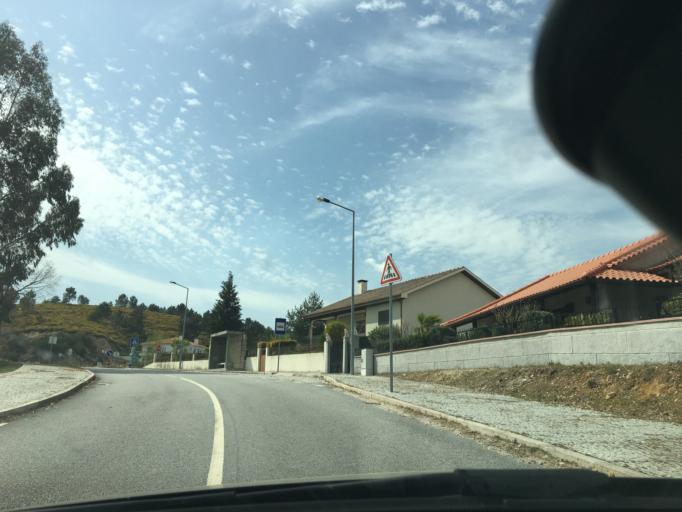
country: PT
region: Vila Real
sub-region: Boticas
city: Boticas
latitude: 41.6862
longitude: -7.7243
